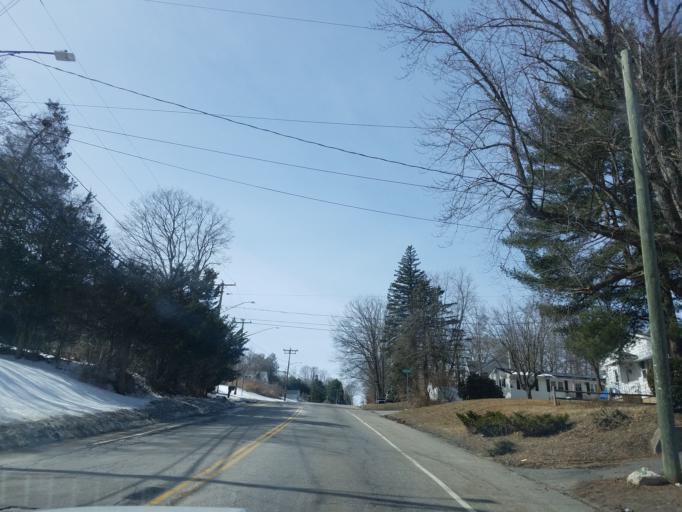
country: US
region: Connecticut
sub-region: Litchfield County
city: Torrington
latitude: 41.8041
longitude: -73.1366
